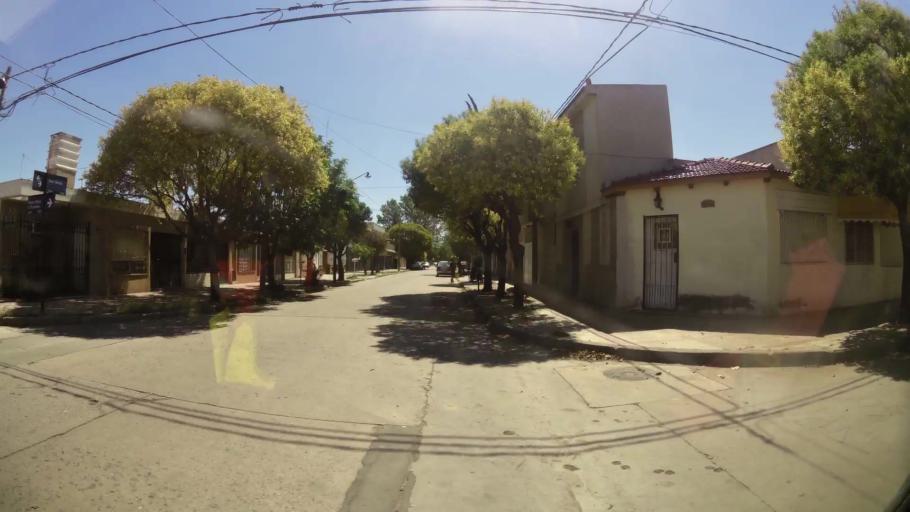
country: AR
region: Cordoba
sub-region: Departamento de Capital
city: Cordoba
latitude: -31.3743
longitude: -64.1431
